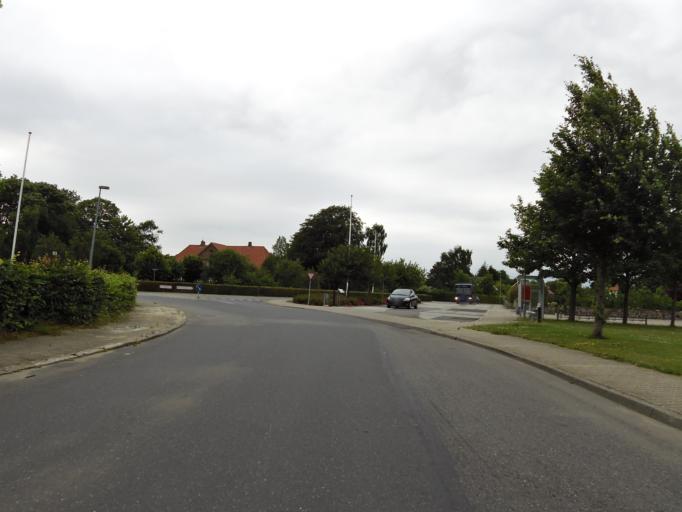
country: DK
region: South Denmark
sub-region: Tonder Kommune
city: Logumkloster
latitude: 55.0755
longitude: 8.9304
